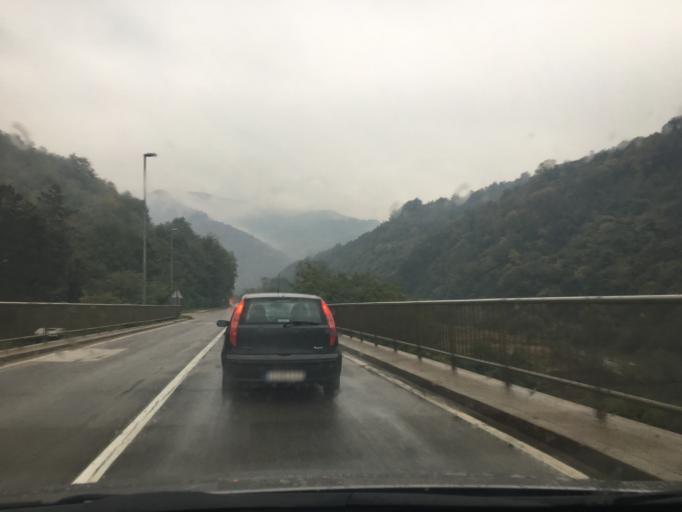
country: RS
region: Central Serbia
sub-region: Pcinjski Okrug
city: Vladicin Han
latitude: 42.7502
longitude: 22.0686
